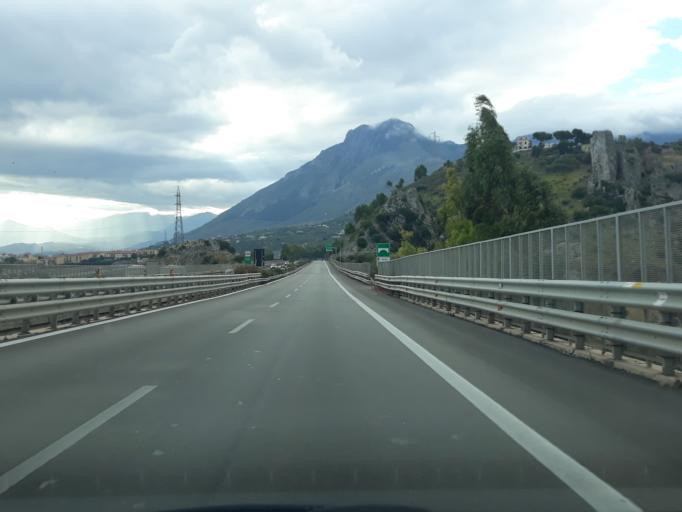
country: IT
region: Sicily
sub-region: Palermo
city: Termini Imerese
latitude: 37.9804
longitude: 13.6703
